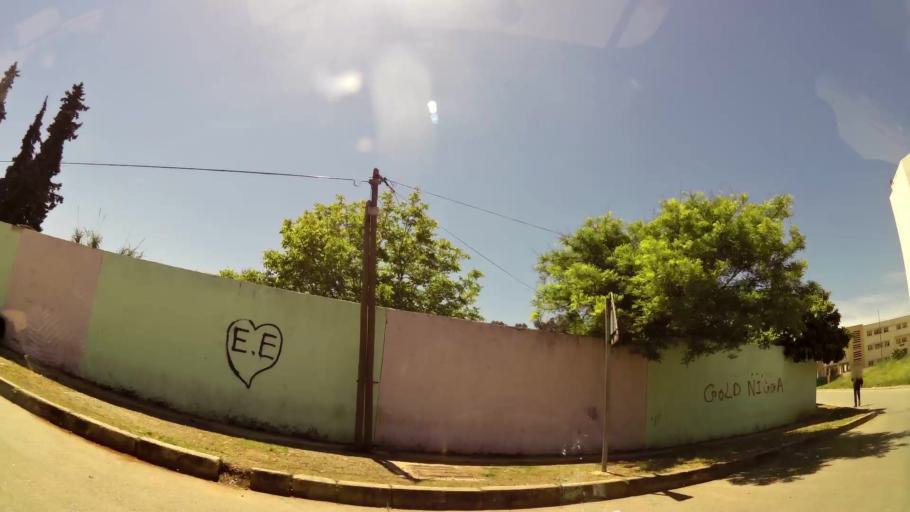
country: MA
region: Meknes-Tafilalet
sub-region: Meknes
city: Meknes
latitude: 33.9013
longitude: -5.5310
